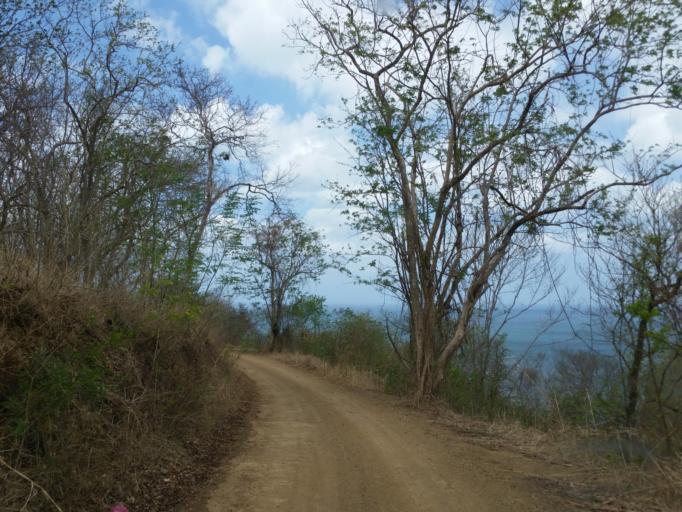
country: NI
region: Rivas
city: Tola
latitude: 11.4231
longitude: -86.0684
